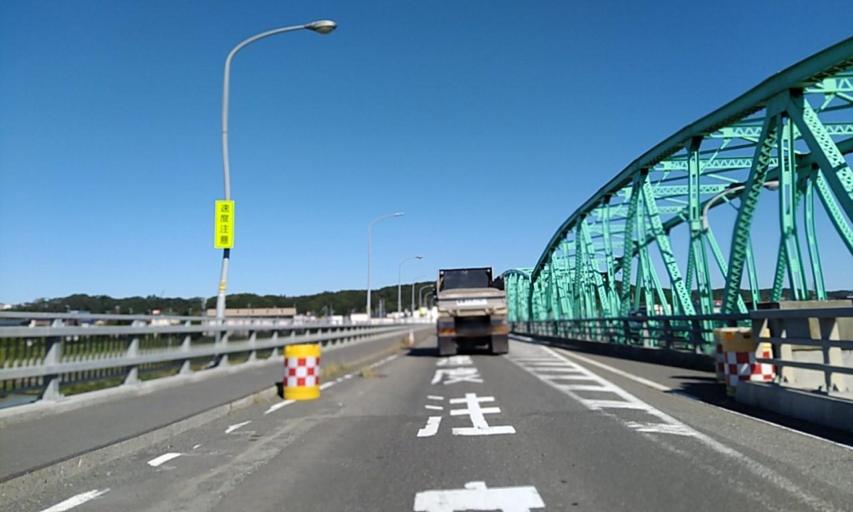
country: JP
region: Hokkaido
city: Shizunai-furukawacho
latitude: 42.5159
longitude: 142.0327
